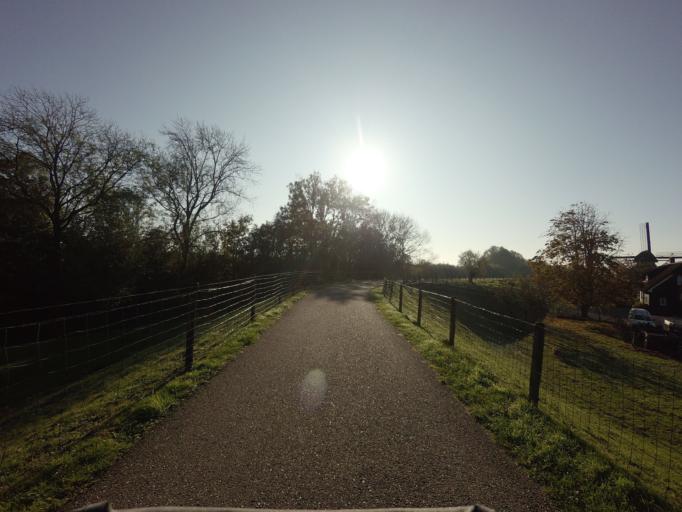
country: NL
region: North Brabant
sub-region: Gemeente Werkendam
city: Werkendam
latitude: 51.8023
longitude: 4.9173
